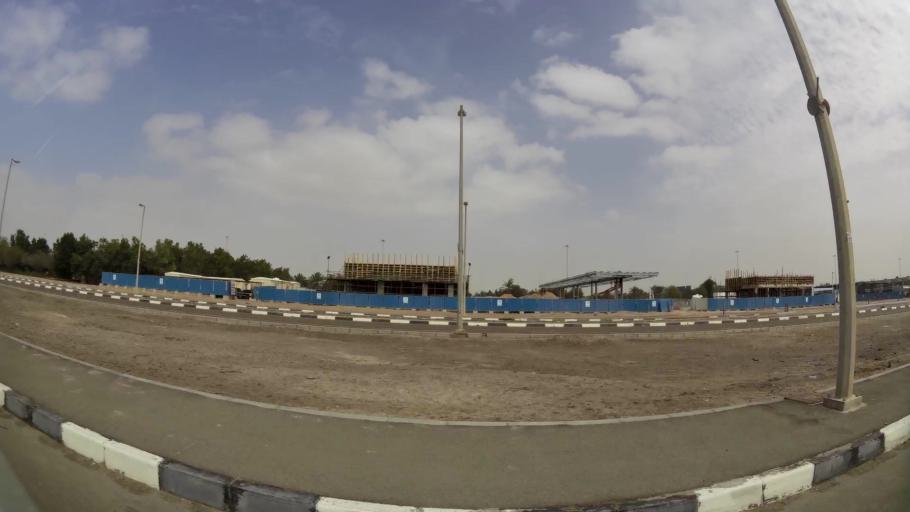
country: AE
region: Abu Dhabi
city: Abu Dhabi
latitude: 24.3955
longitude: 54.5081
